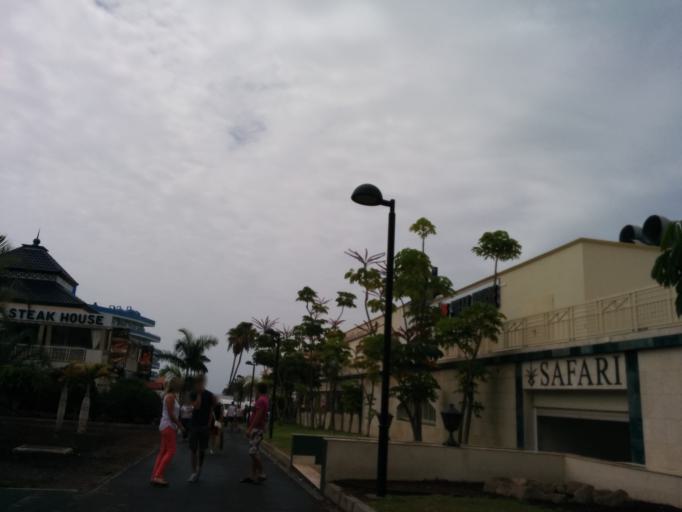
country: ES
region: Canary Islands
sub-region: Provincia de Santa Cruz de Tenerife
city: Playa de las Americas
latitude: 28.0555
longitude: -16.7302
